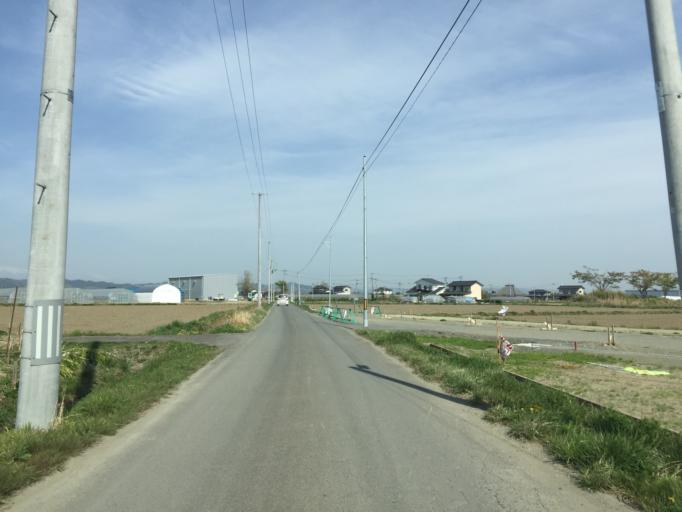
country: JP
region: Miyagi
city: Watari
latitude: 38.0244
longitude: 140.9021
